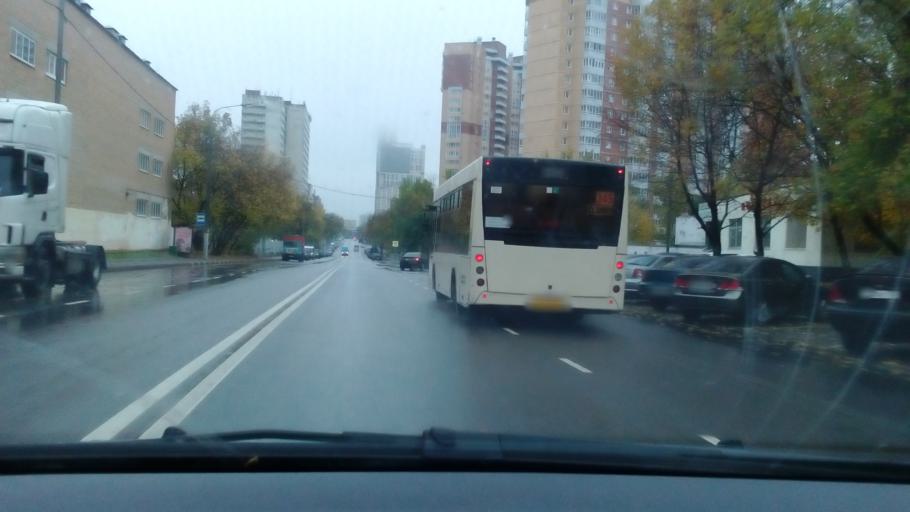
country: RU
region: Moskovskaya
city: Levoberezhnaya
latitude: 55.8707
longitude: 37.4716
